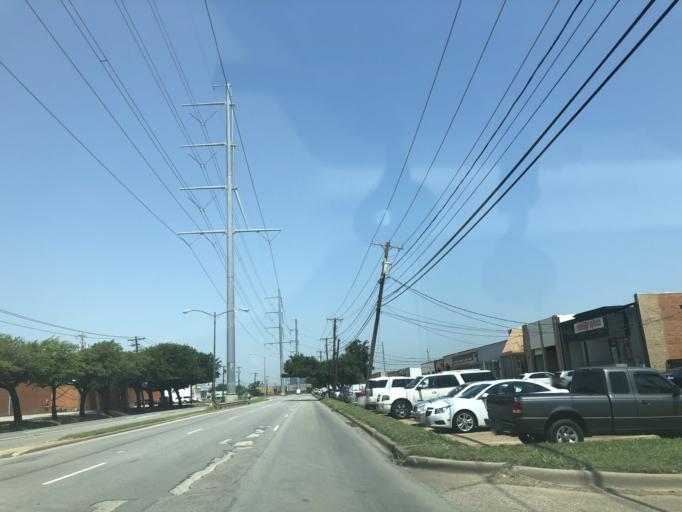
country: US
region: Texas
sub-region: Dallas County
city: Dallas
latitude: 32.7975
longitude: -96.8379
